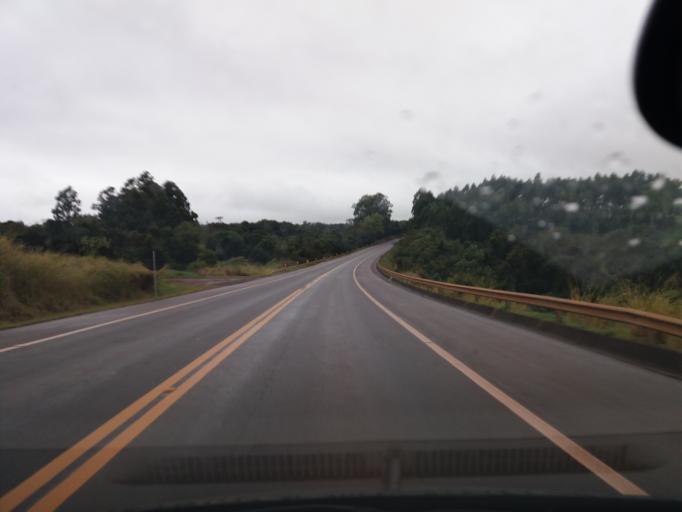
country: BR
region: Parana
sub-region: Campo Mourao
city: Campo Mourao
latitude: -24.3217
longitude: -52.6442
